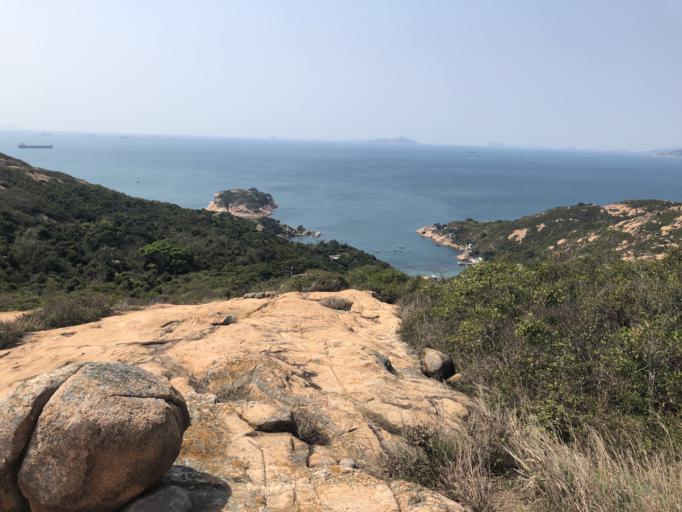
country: HK
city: Sok Kwu Wan
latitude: 22.1661
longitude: 114.2598
